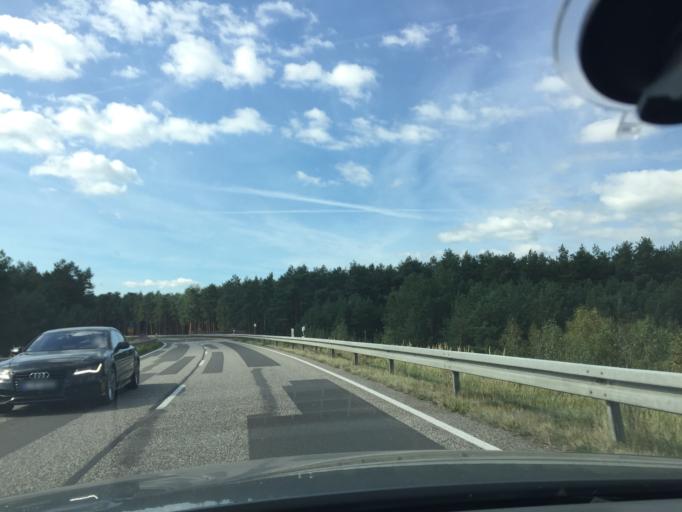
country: DE
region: Brandenburg
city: Grunheide
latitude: 52.3936
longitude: 13.8033
